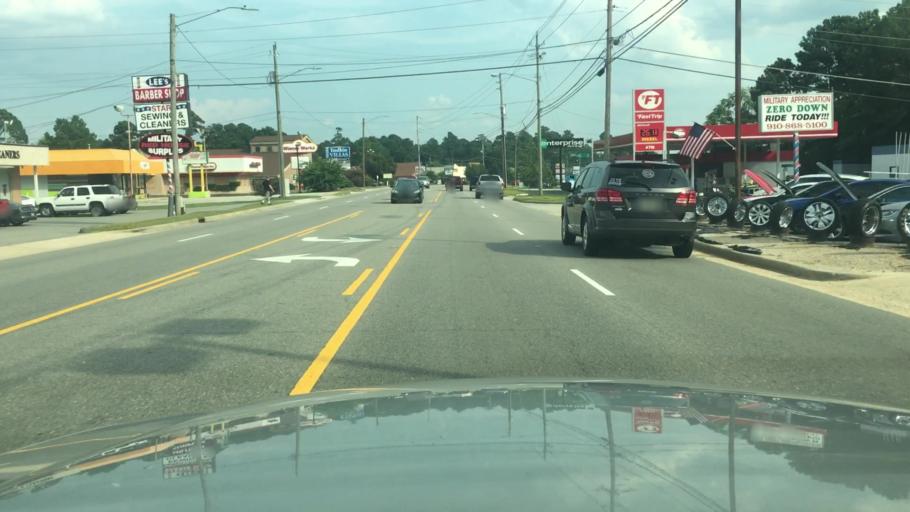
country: US
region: North Carolina
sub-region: Cumberland County
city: Fort Bragg
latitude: 35.1018
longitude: -78.9914
